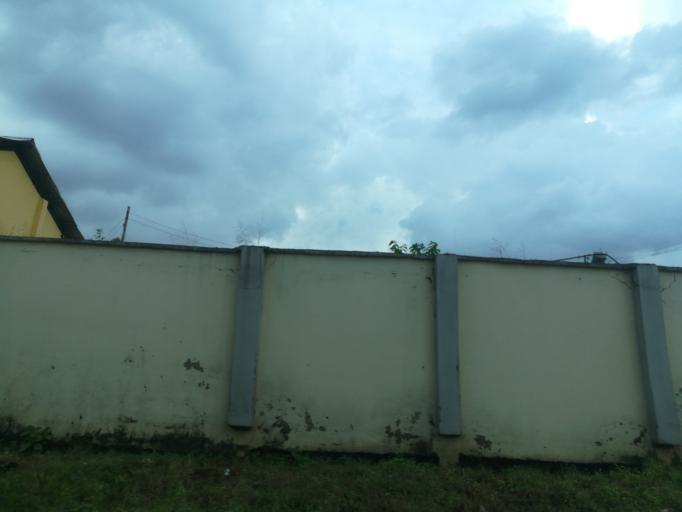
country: NG
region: Oyo
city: Ibadan
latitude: 7.4520
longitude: 3.9022
